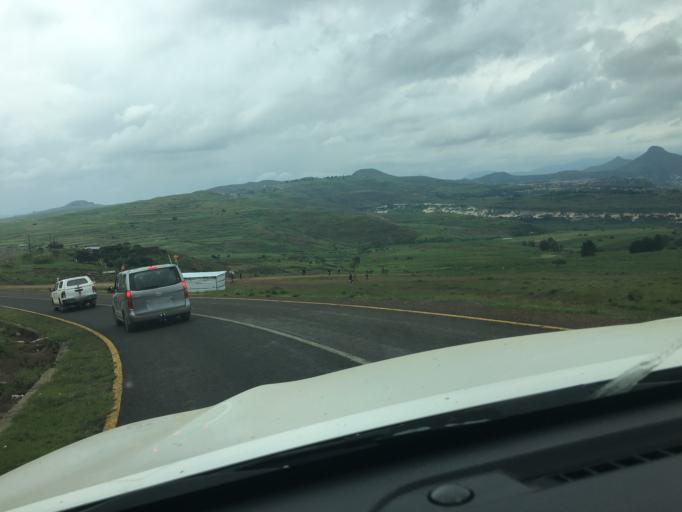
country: LS
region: Berea
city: Teyateyaneng
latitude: -29.2550
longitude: 27.8462
